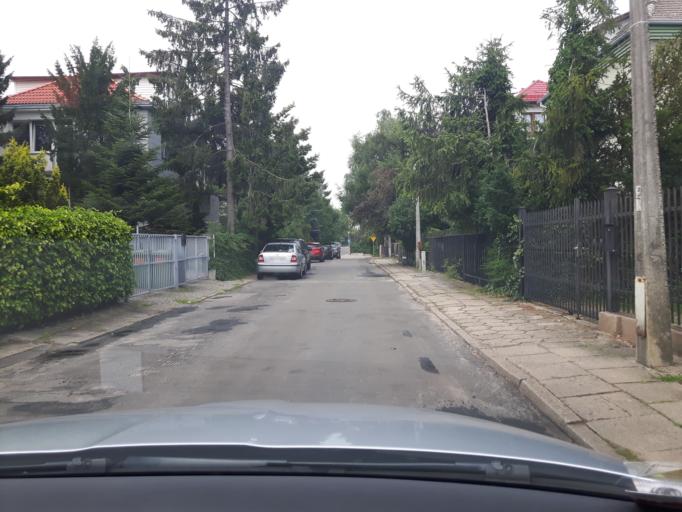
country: PL
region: Pomeranian Voivodeship
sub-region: Sopot
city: Sopot
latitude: 54.4321
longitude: 18.5750
